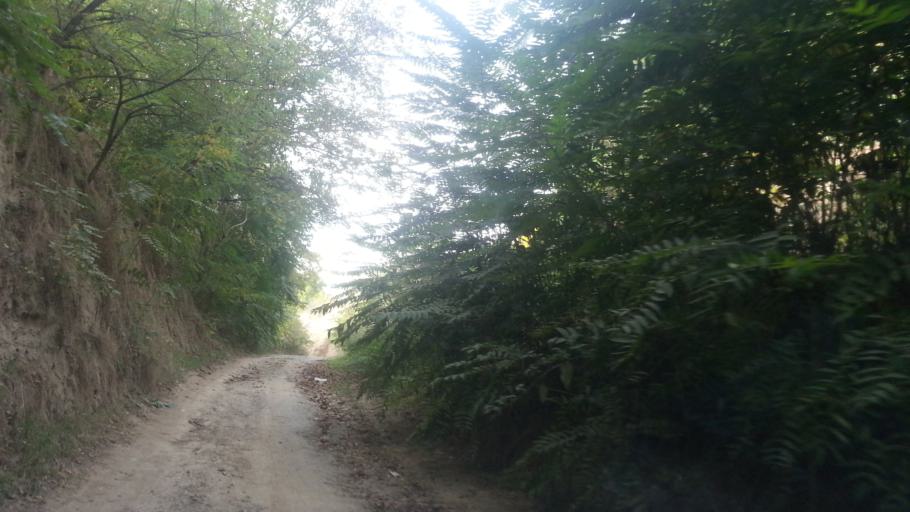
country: RS
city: Belegis
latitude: 45.0214
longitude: 20.3465
